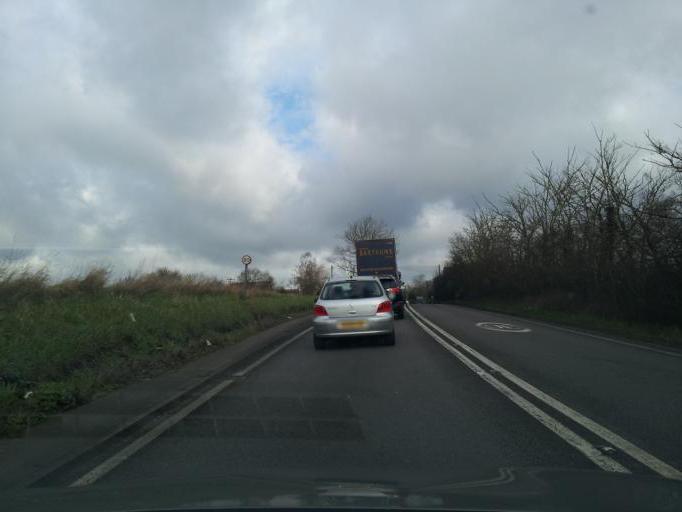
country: GB
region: England
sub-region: Suffolk
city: Needham Market
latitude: 52.1946
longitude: 1.0979
